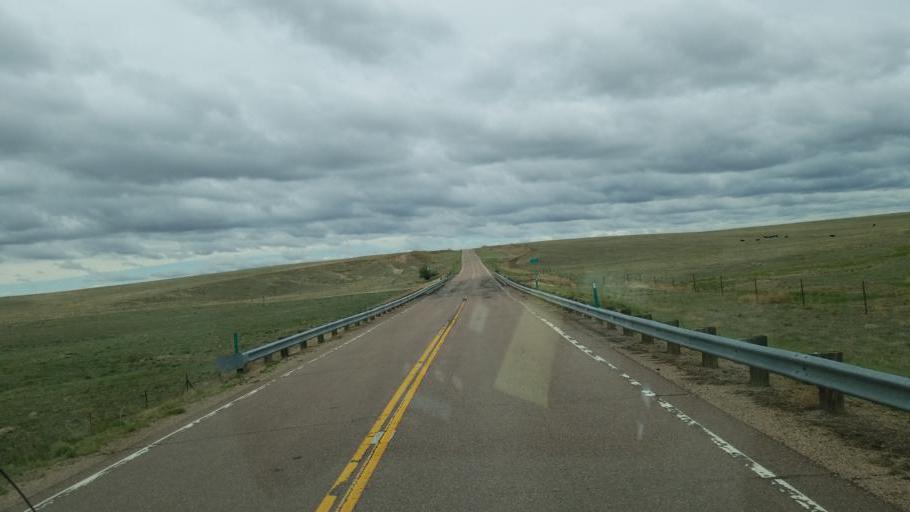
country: US
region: Colorado
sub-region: Lincoln County
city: Limon
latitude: 38.8392
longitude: -103.9042
